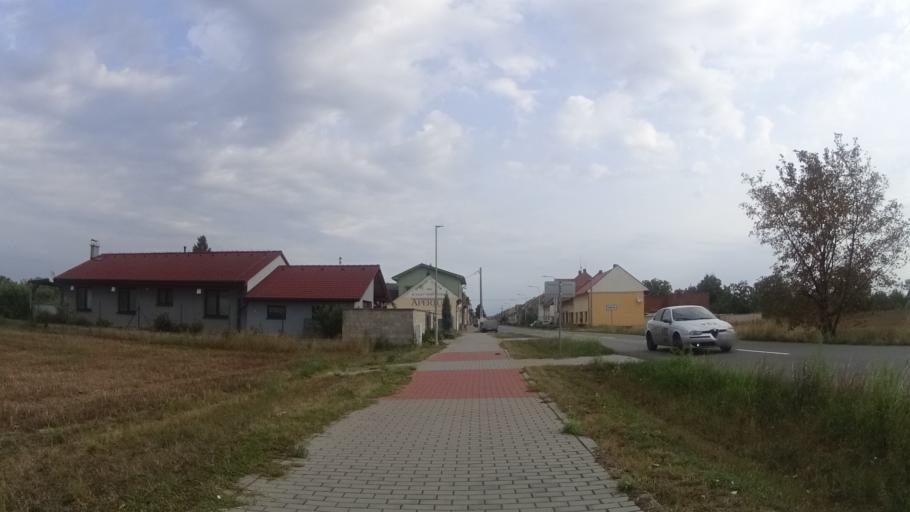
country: CZ
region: Zlin
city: Chropyne
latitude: 49.3497
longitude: 17.3751
